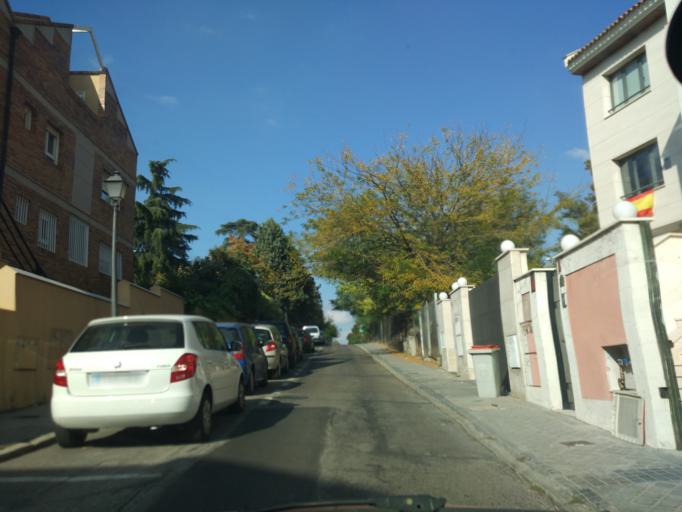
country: ES
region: Madrid
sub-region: Provincia de Madrid
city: Tetuan de las Victorias
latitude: 40.4617
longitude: -3.7244
